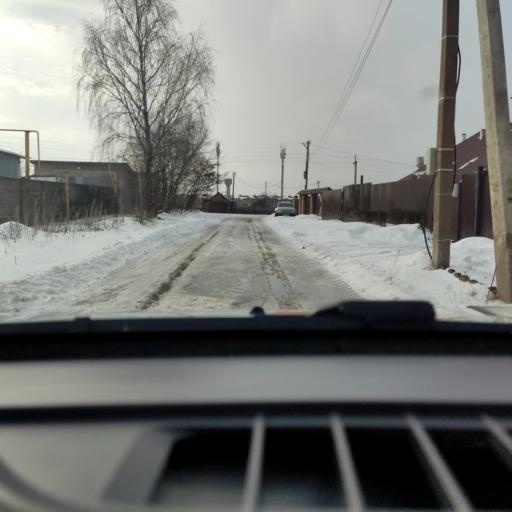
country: RU
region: Voronezj
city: Podgornoye
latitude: 51.7736
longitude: 39.1281
